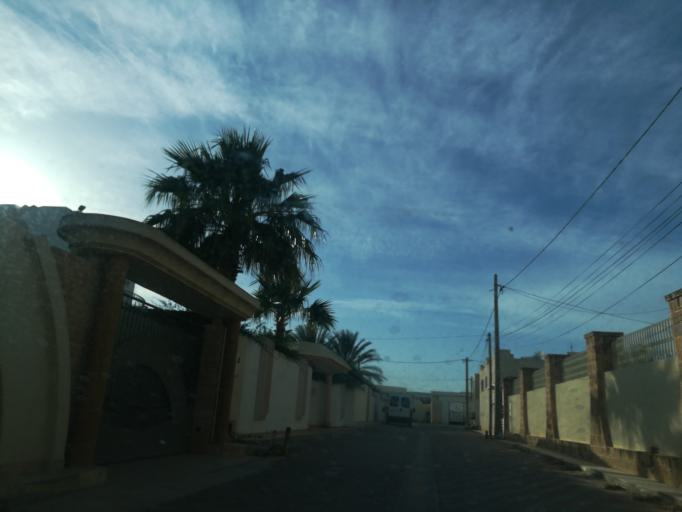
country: TN
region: Safaqis
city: Al Qarmadah
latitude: 34.8086
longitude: 10.7555
